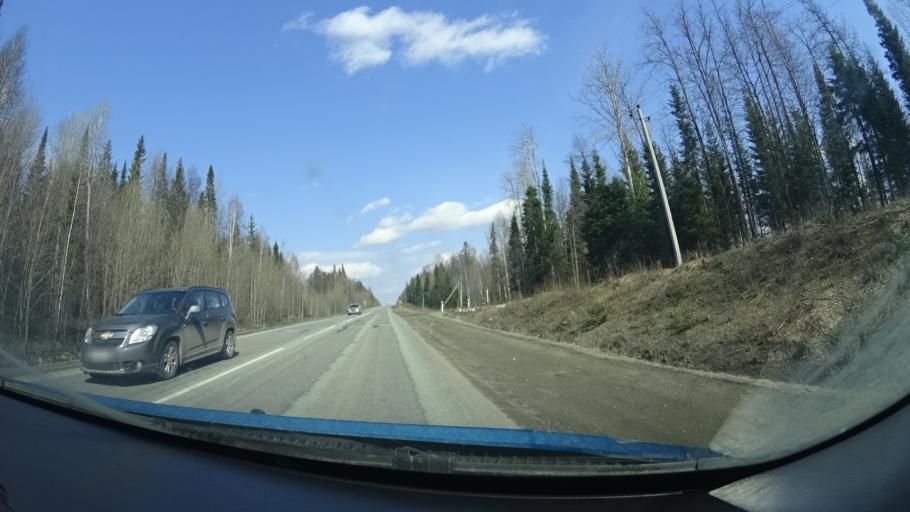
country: RU
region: Perm
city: Kultayevo
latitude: 57.8115
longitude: 55.7911
